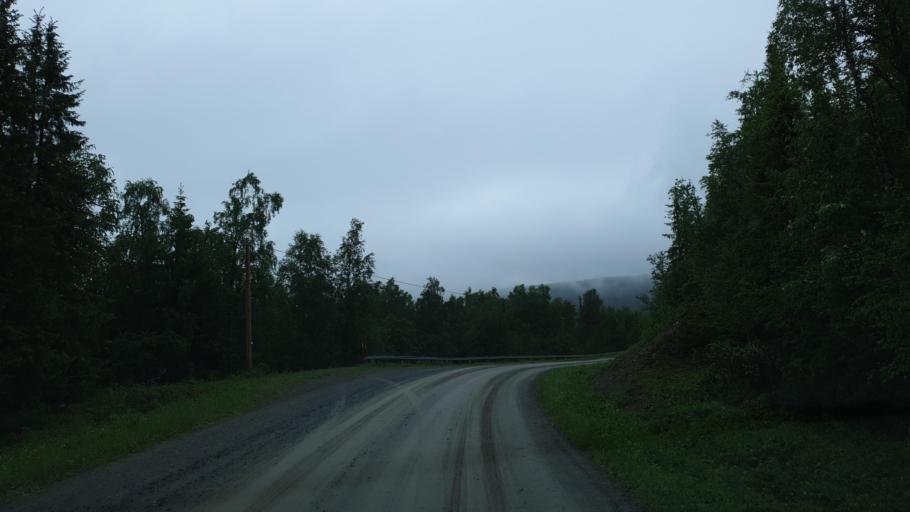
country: SE
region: Vaesterbotten
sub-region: Vilhelmina Kommun
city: Sjoberg
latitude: 65.3329
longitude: 15.8684
